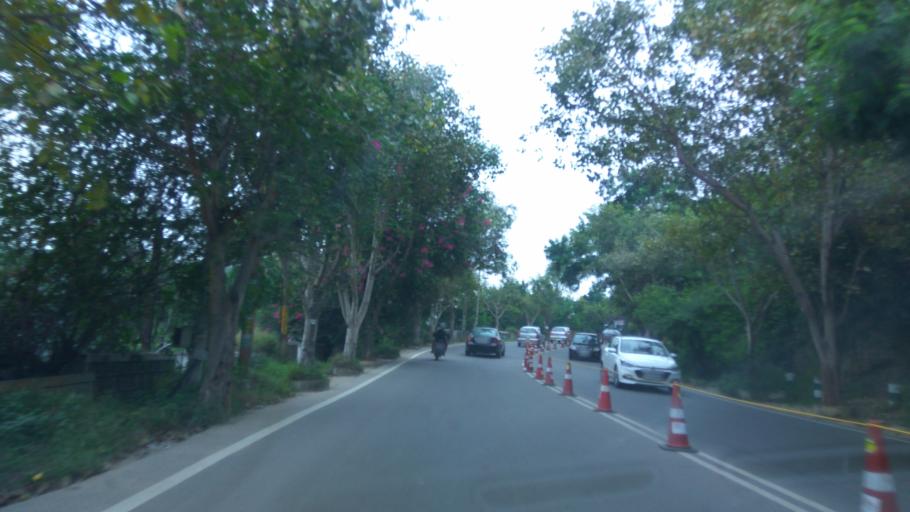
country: IN
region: Telangana
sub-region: Rangareddi
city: Kukatpalli
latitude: 17.4328
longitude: 78.3884
